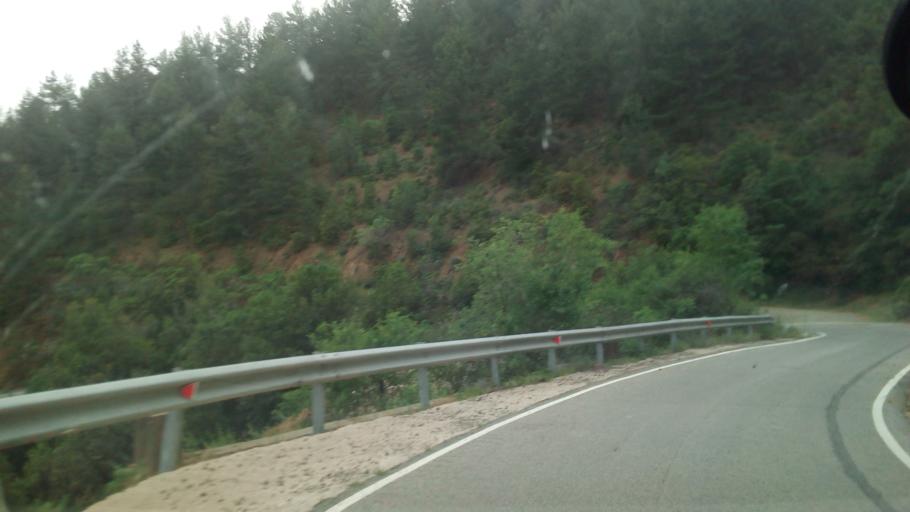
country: CY
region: Lefkosia
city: Kakopetria
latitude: 34.9683
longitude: 32.7480
